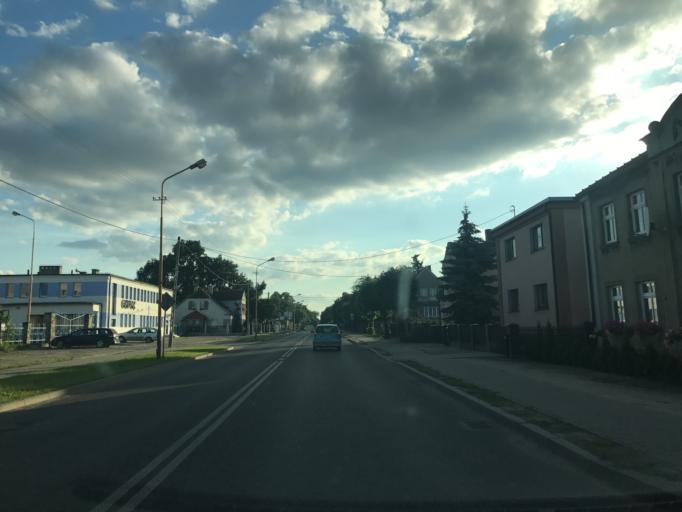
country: PL
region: Greater Poland Voivodeship
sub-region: Powiat jarocinski
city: Jarocin
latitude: 51.9718
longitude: 17.4919
